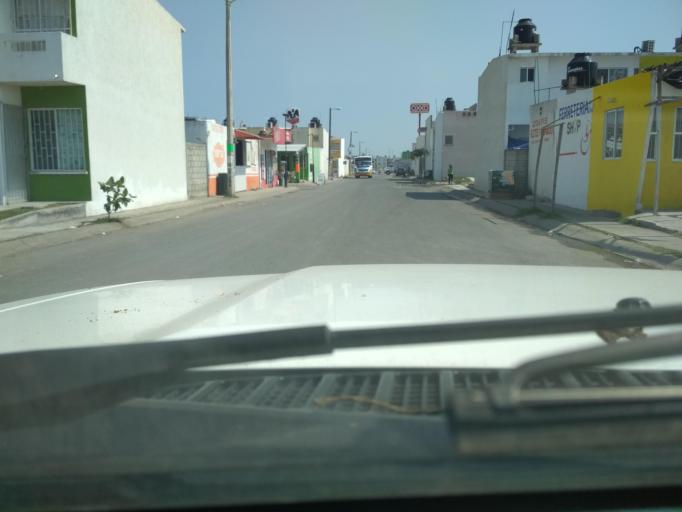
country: MX
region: Veracruz
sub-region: Veracruz
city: Lomas de Rio Medio Cuatro
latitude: 19.1898
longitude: -96.2096
